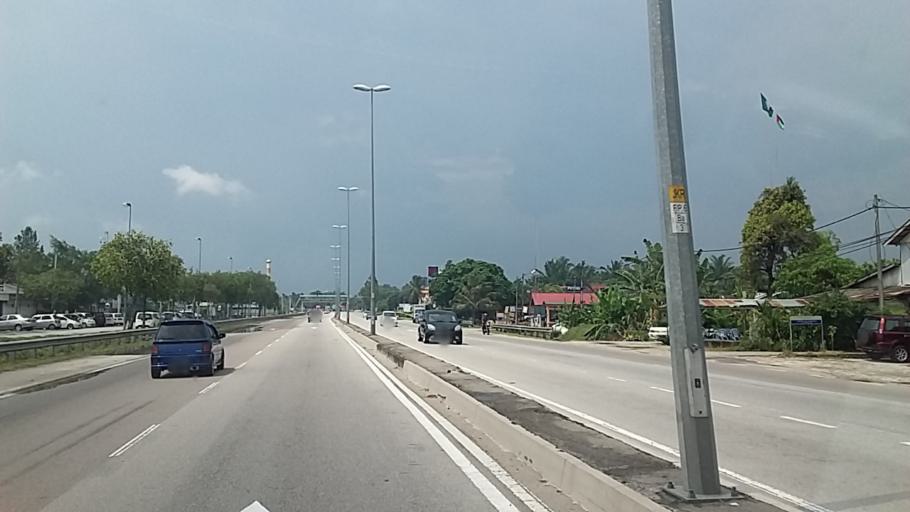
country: MY
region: Johor
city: Parit Raja
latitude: 1.8555
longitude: 103.0954
